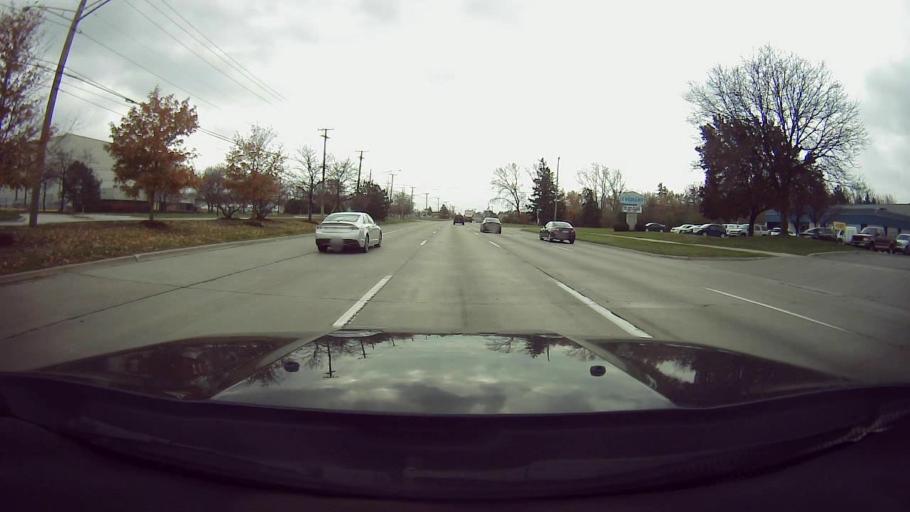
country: US
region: Michigan
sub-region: Macomb County
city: Sterling Heights
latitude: 42.5403
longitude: -83.0481
